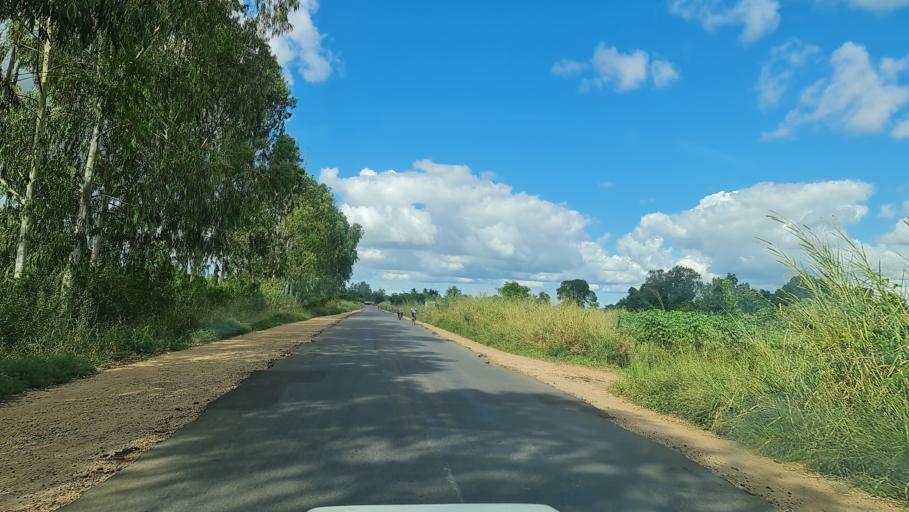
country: MZ
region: Zambezia
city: Quelimane
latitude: -17.5998
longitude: 36.7977
